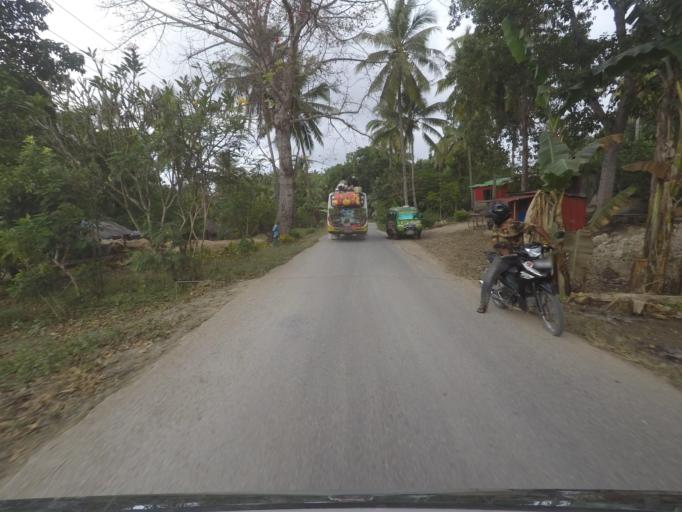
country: TL
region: Baucau
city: Baucau
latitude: -8.5151
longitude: 126.4395
